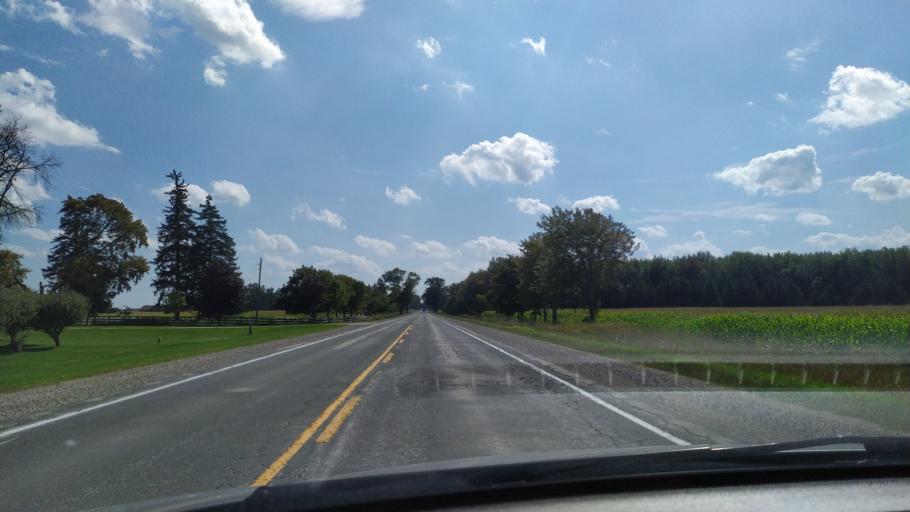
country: CA
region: Ontario
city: Stratford
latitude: 43.3273
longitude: -80.9908
